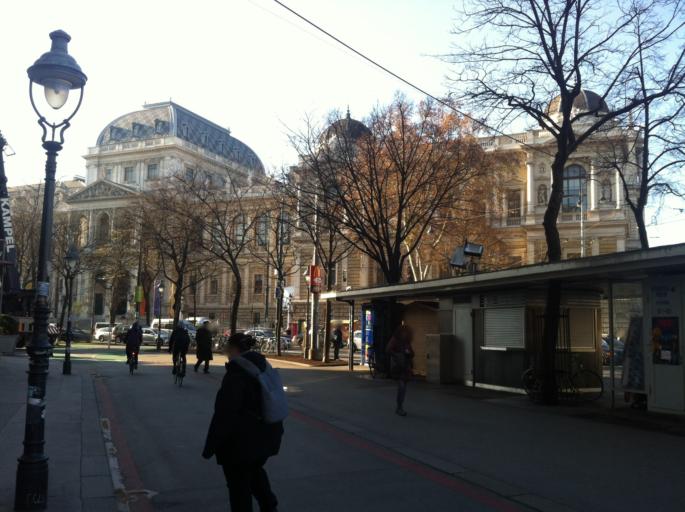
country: AT
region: Vienna
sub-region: Wien Stadt
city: Vienna
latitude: 48.2136
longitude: 16.3621
